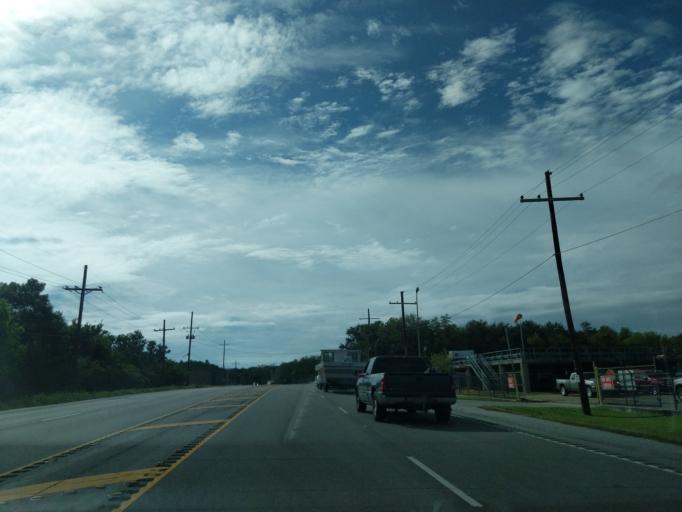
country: US
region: Louisiana
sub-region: Saint Tammany Parish
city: Eden Isle
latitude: 30.0767
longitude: -89.8545
